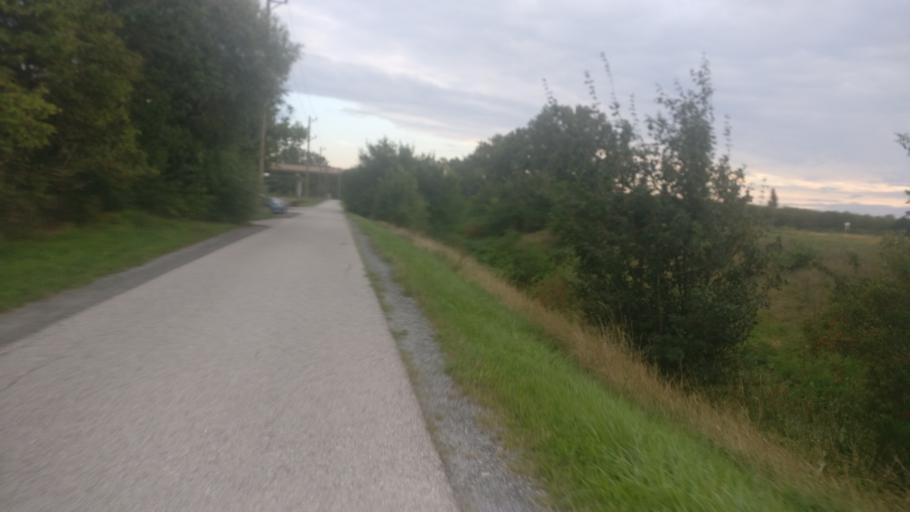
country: AT
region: Lower Austria
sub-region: Politischer Bezirk Wien-Umgebung
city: Lanzendorf
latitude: 48.0968
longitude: 16.4416
